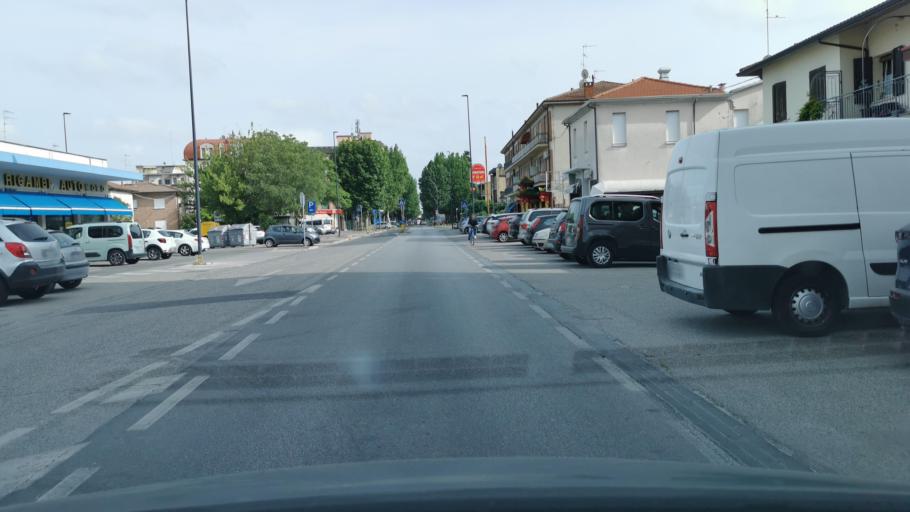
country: IT
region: Emilia-Romagna
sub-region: Provincia di Ravenna
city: Ravenna
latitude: 44.4092
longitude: 12.2077
